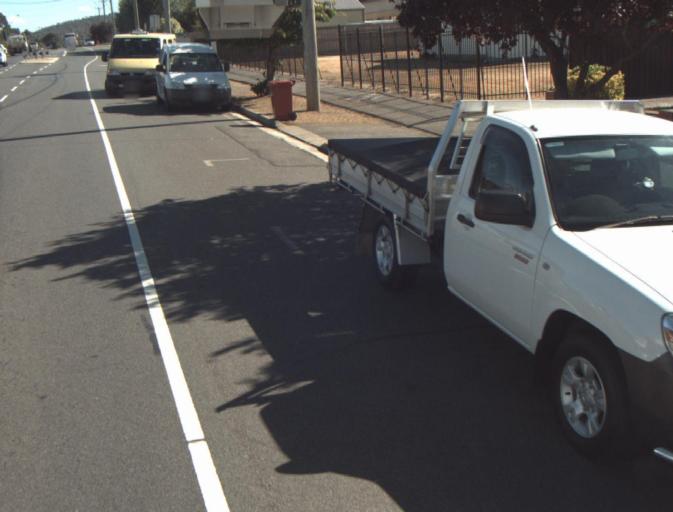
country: AU
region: Tasmania
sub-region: Launceston
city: Mayfield
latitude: -41.3852
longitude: 147.1279
